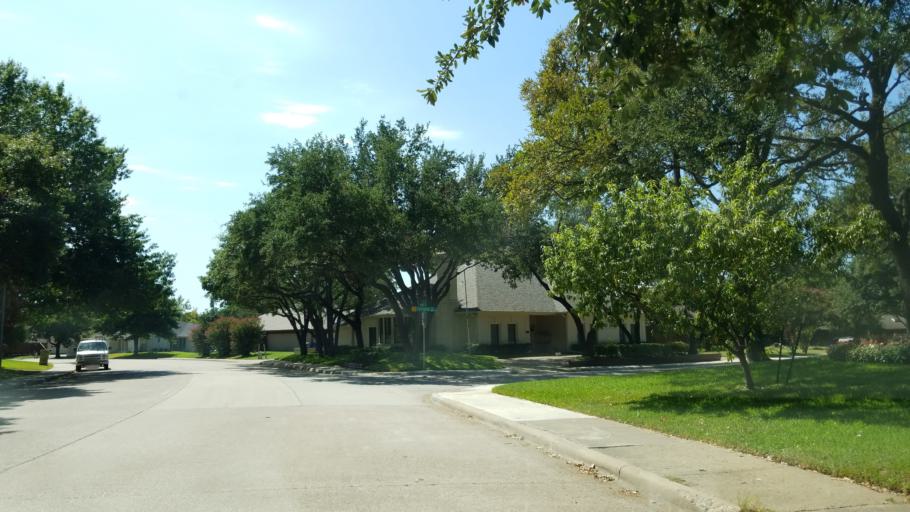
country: US
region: Texas
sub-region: Dallas County
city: Addison
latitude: 32.9703
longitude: -96.7907
